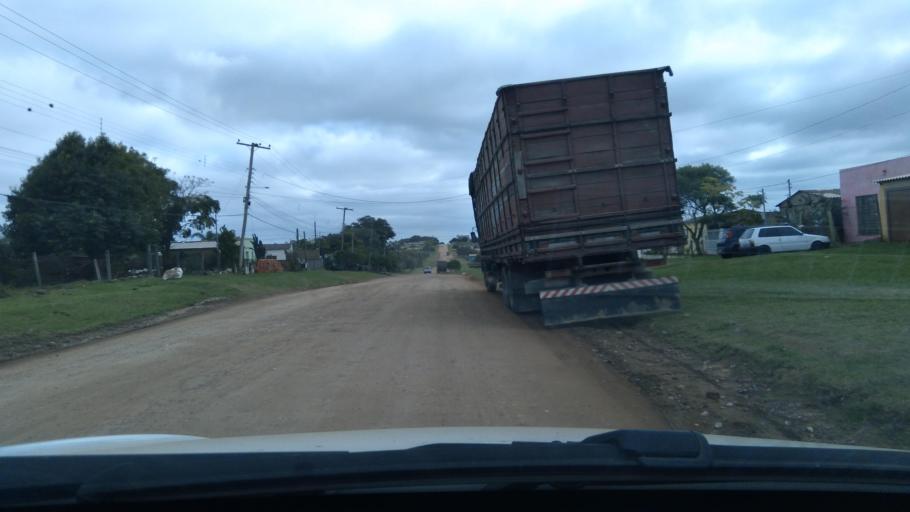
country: BR
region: Rio Grande do Sul
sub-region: Dom Pedrito
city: Dom Pedrito
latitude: -30.9820
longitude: -54.6495
